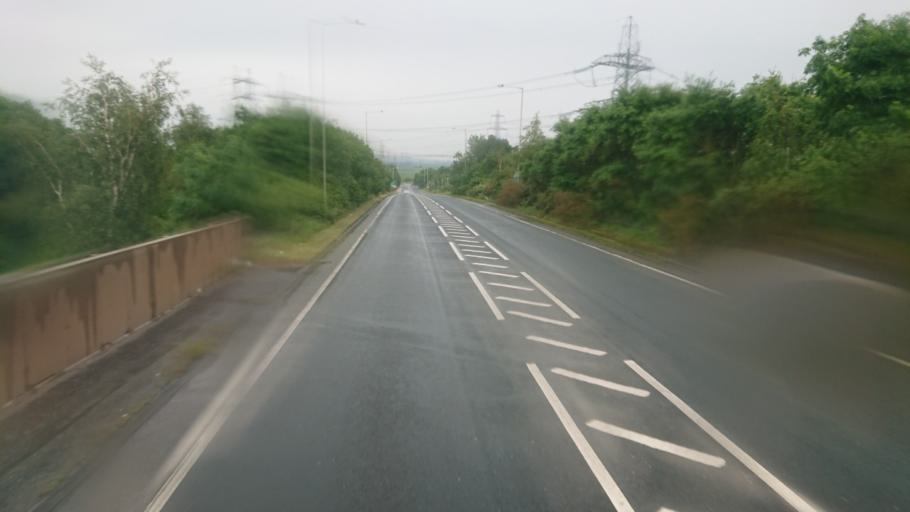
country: GB
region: England
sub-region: Lancashire
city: Morecambe
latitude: 54.0343
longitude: -2.8917
